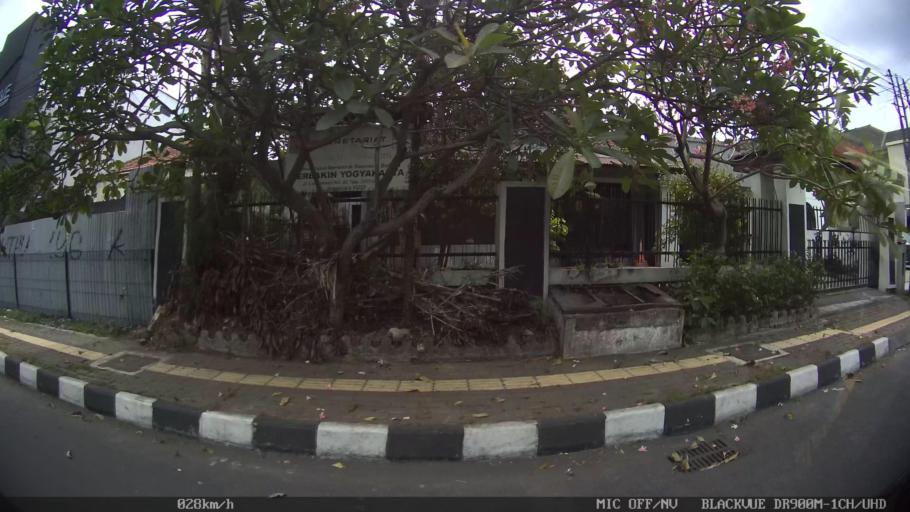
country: ID
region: Daerah Istimewa Yogyakarta
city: Yogyakarta
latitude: -7.7861
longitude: 110.3846
